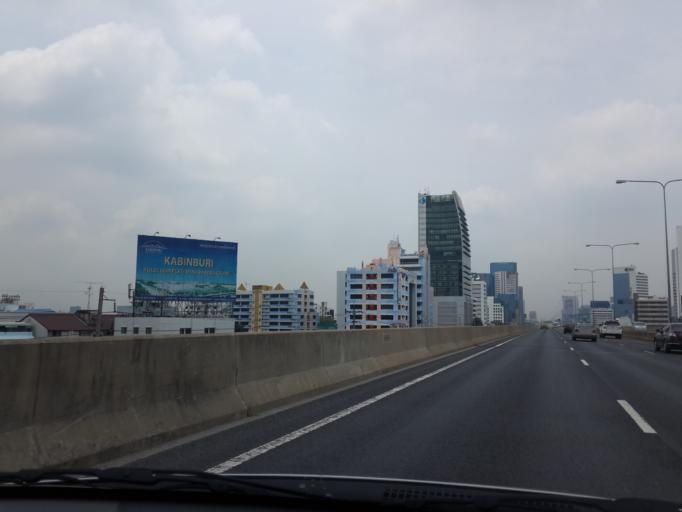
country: TH
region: Bangkok
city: Phaya Thai
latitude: 13.7959
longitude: 100.5610
